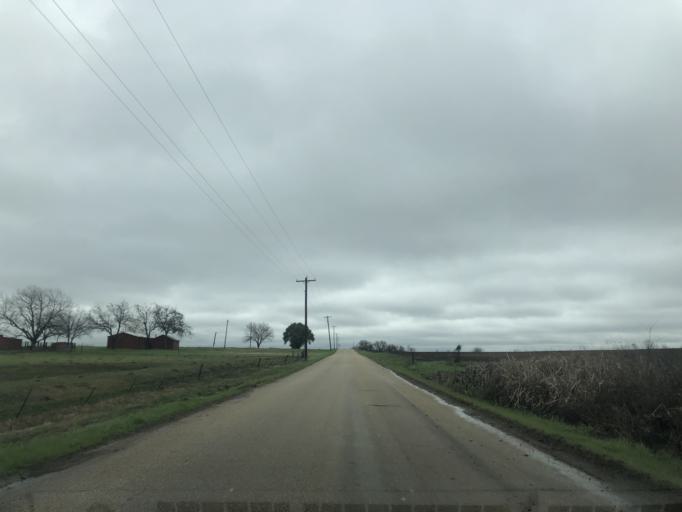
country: US
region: Texas
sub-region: Williamson County
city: Hutto
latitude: 30.5804
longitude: -97.4958
